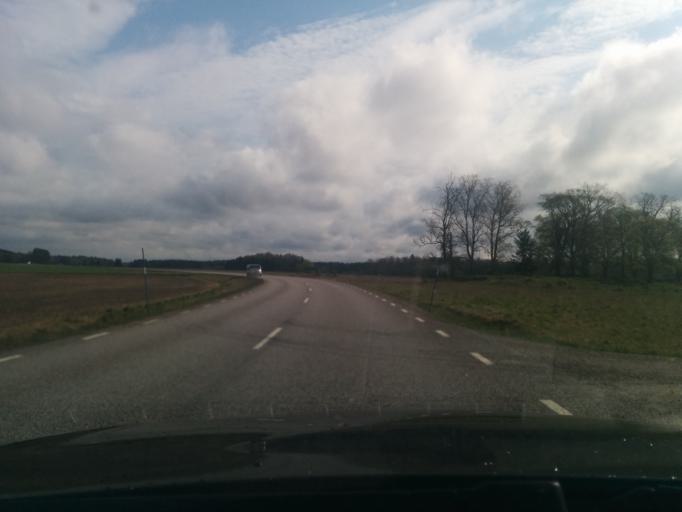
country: SE
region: Uppsala
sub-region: Tierps Kommun
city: Orbyhus
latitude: 60.1773
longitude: 17.6581
